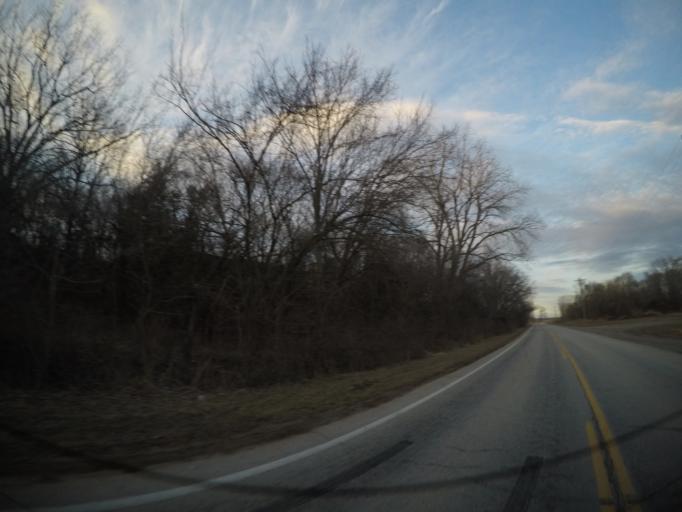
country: US
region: Kansas
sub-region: Wyandotte County
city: Bonner Springs
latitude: 39.0122
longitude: -94.9120
